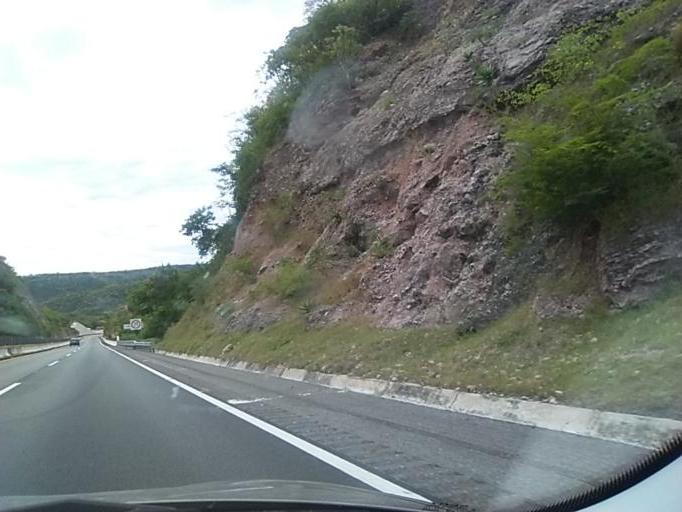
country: MX
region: Guerrero
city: Copalillo
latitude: 18.1194
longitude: -99.2066
